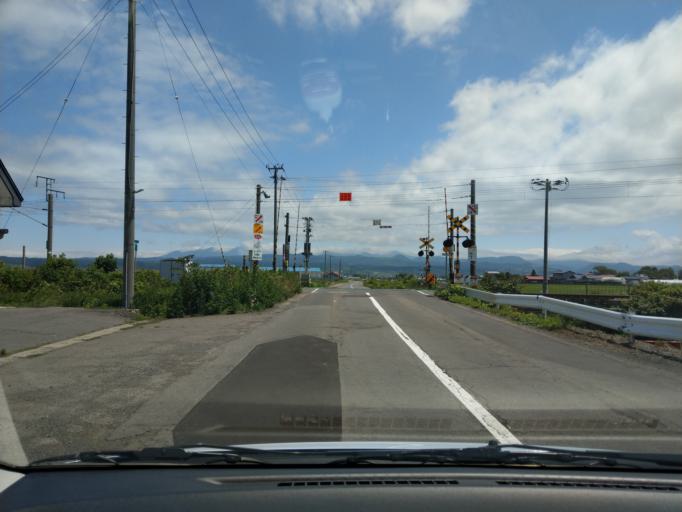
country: JP
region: Aomori
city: Namioka
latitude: 40.6842
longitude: 140.5559
